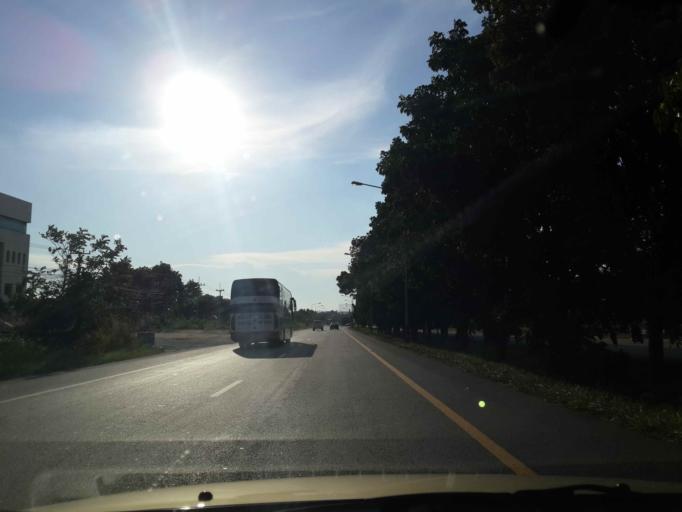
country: TH
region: Chon Buri
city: Bang Lamung
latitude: 12.9886
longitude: 100.9444
